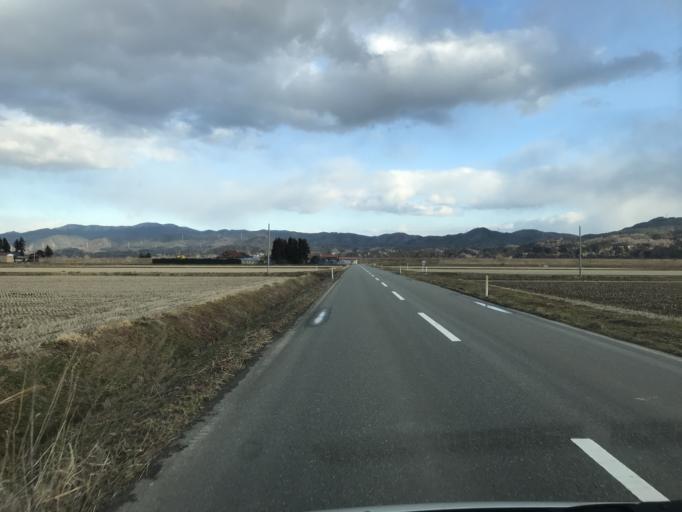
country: JP
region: Iwate
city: Mizusawa
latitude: 39.0577
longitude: 141.1475
